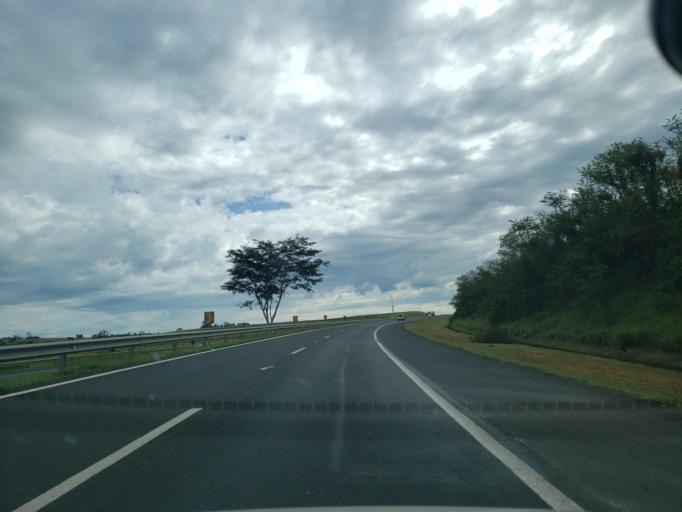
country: BR
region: Sao Paulo
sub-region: Bauru
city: Bauru
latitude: -22.1958
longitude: -49.1991
